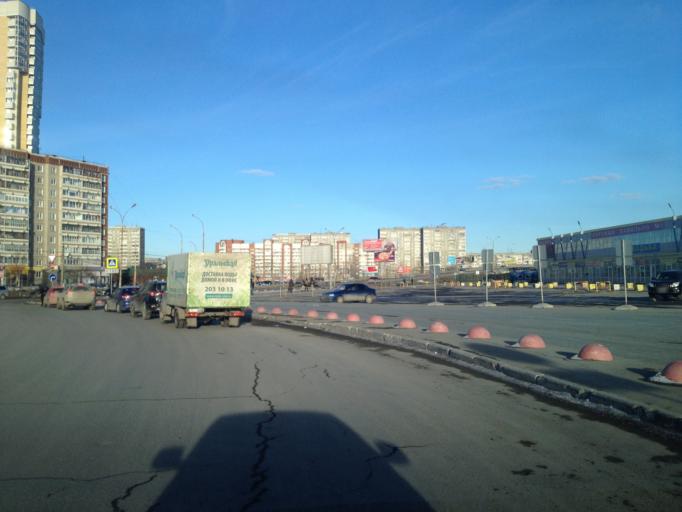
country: RU
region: Sverdlovsk
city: Yekaterinburg
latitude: 56.8616
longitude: 60.5431
